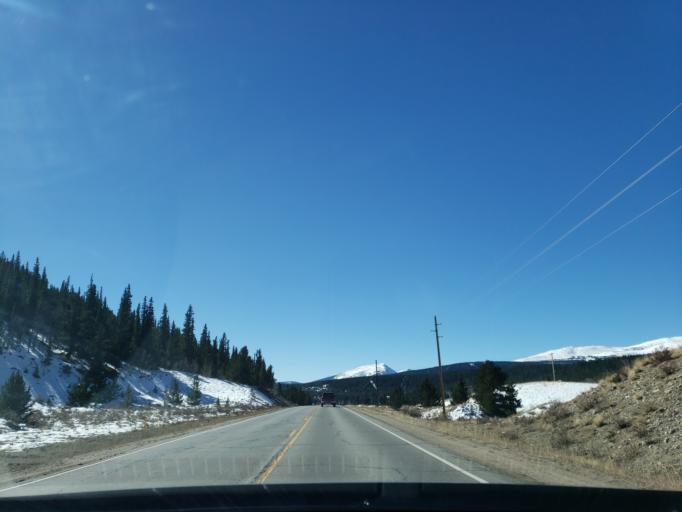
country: US
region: Colorado
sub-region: Park County
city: Fairplay
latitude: 39.3047
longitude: -106.0626
